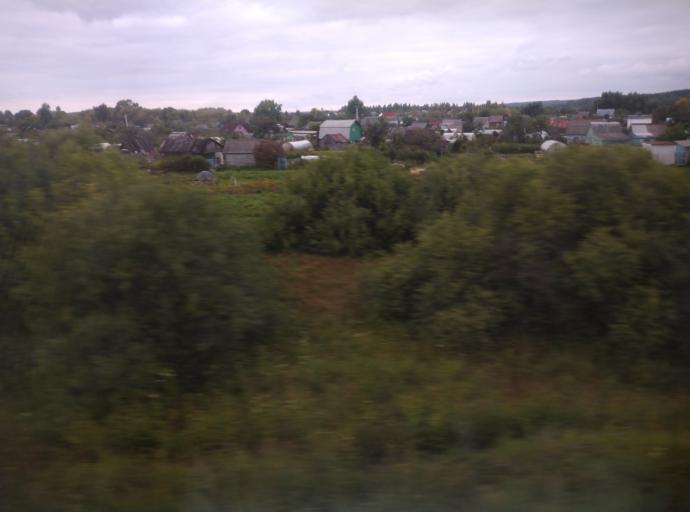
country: RU
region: Kostroma
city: Nerekhta
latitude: 57.4749
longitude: 40.5797
